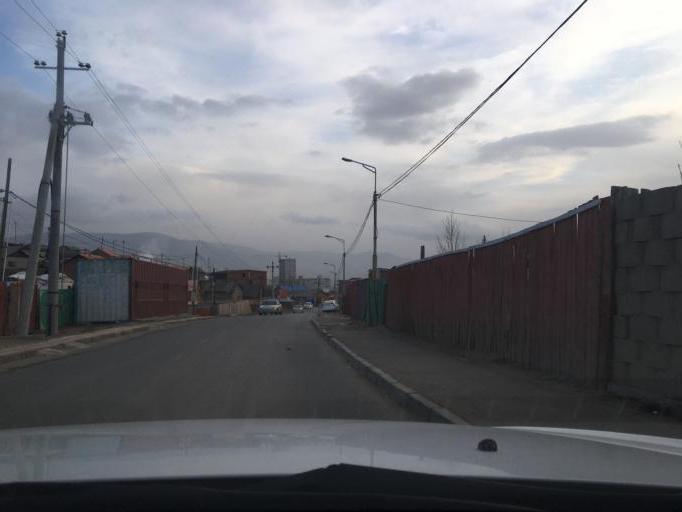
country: MN
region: Ulaanbaatar
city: Ulaanbaatar
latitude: 47.9290
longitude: 106.8586
